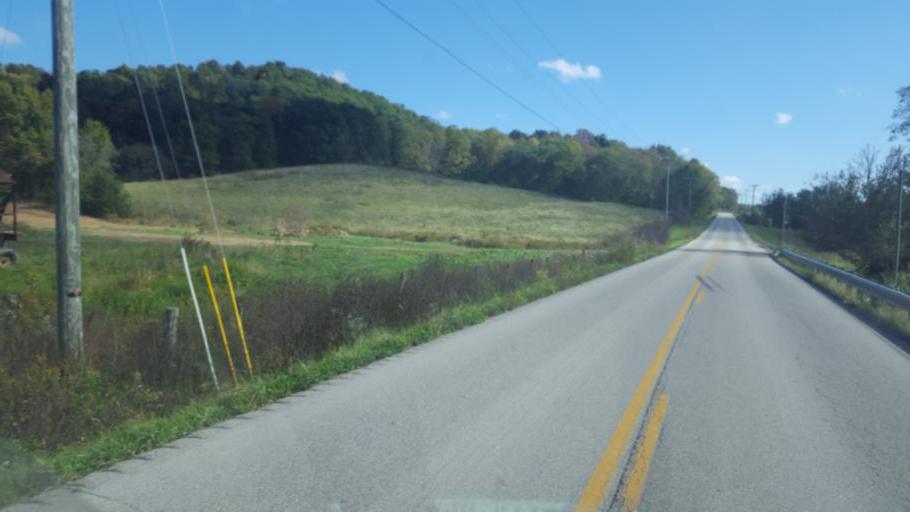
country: US
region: Kentucky
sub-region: Fleming County
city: Flemingsburg
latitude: 38.4702
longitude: -83.5792
